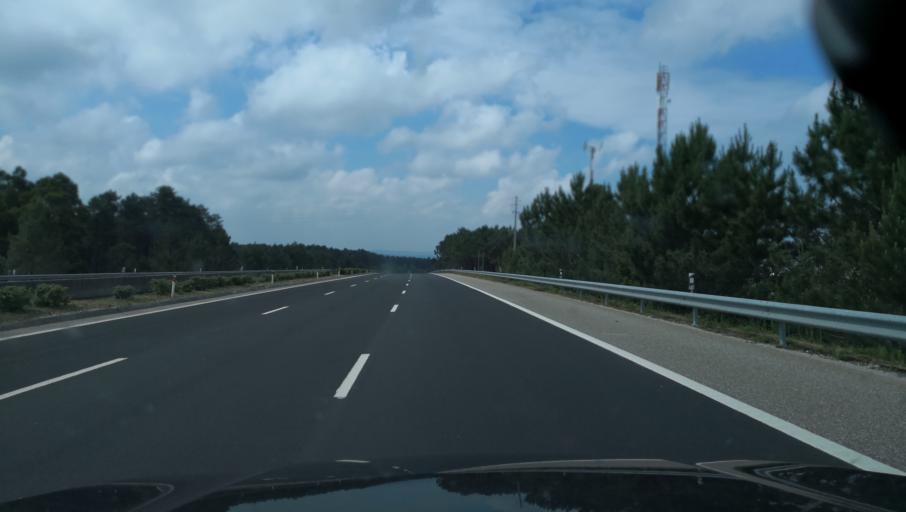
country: PT
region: Leiria
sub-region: Leiria
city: Maceira
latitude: 39.6882
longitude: -8.9334
